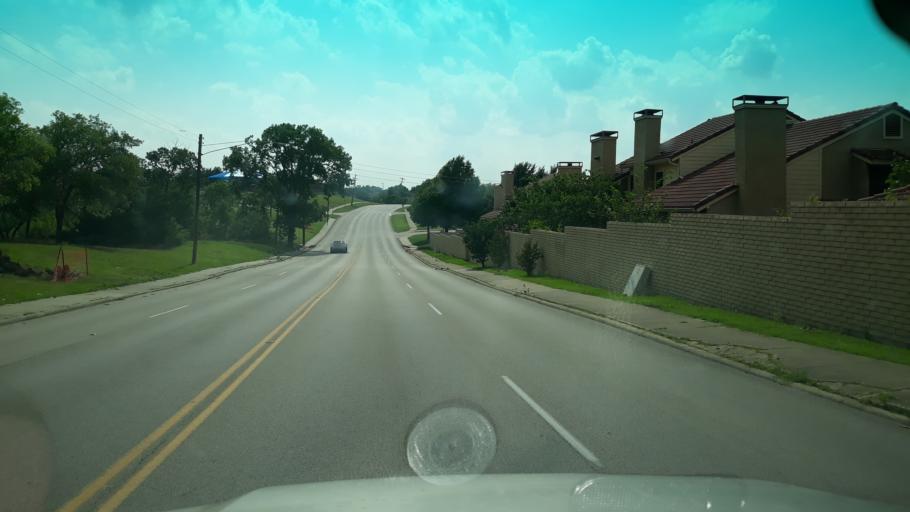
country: US
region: Texas
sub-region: Dallas County
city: Irving
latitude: 32.8596
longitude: -96.9843
